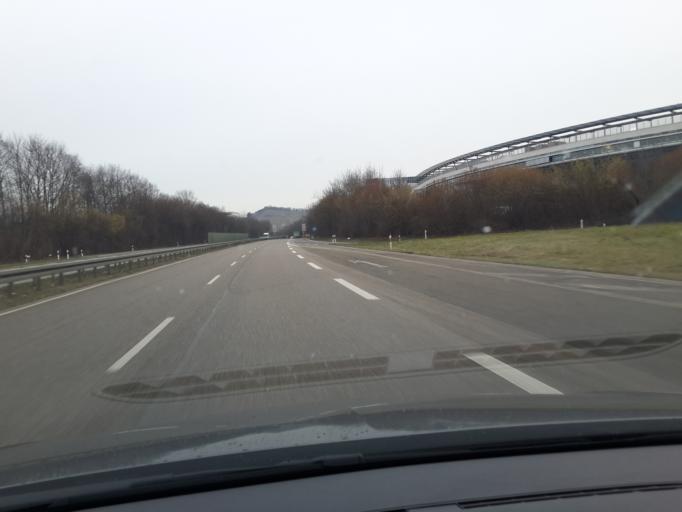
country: DE
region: Baden-Wuerttemberg
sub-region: Regierungsbezirk Stuttgart
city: Neckarsulm
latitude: 49.1815
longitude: 9.2309
